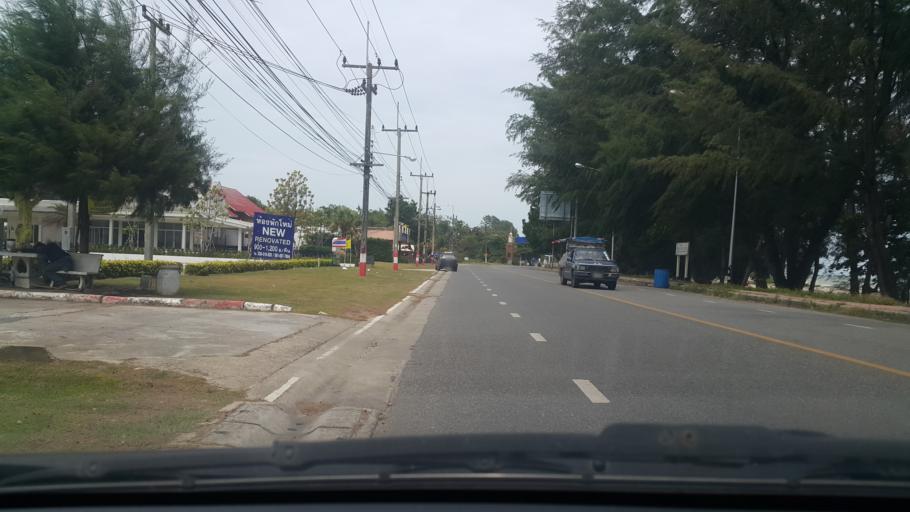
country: TH
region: Rayong
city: Rayong
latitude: 12.6126
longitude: 101.3826
